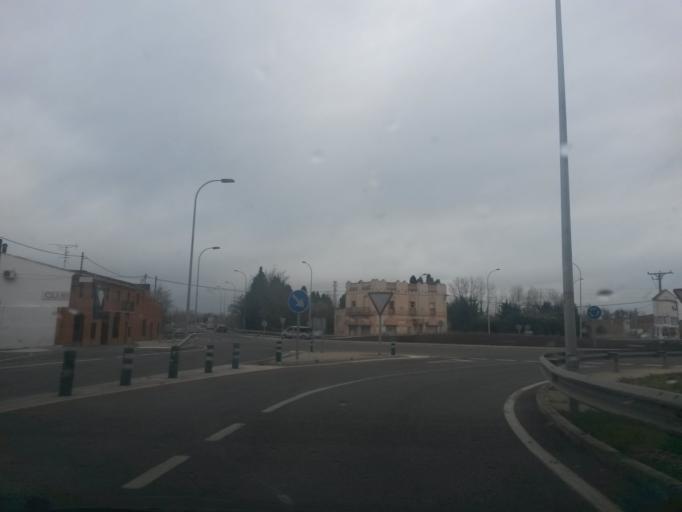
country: ES
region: Catalonia
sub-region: Provincia de Girona
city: Vilamalla
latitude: 42.2363
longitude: 2.9671
